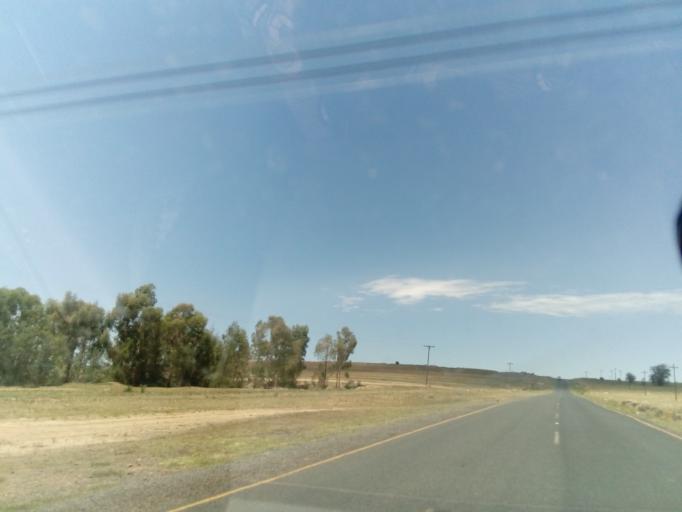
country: LS
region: Berea
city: Teyateyaneng
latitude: -29.1267
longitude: 27.7832
